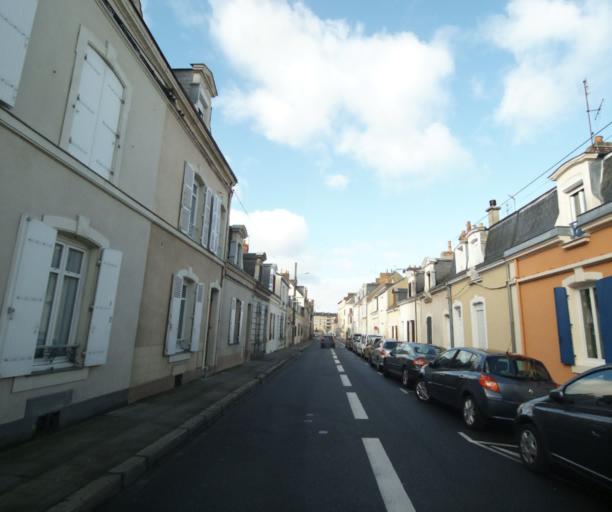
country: FR
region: Pays de la Loire
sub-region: Departement de la Sarthe
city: Le Mans
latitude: 48.0002
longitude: 0.1848
